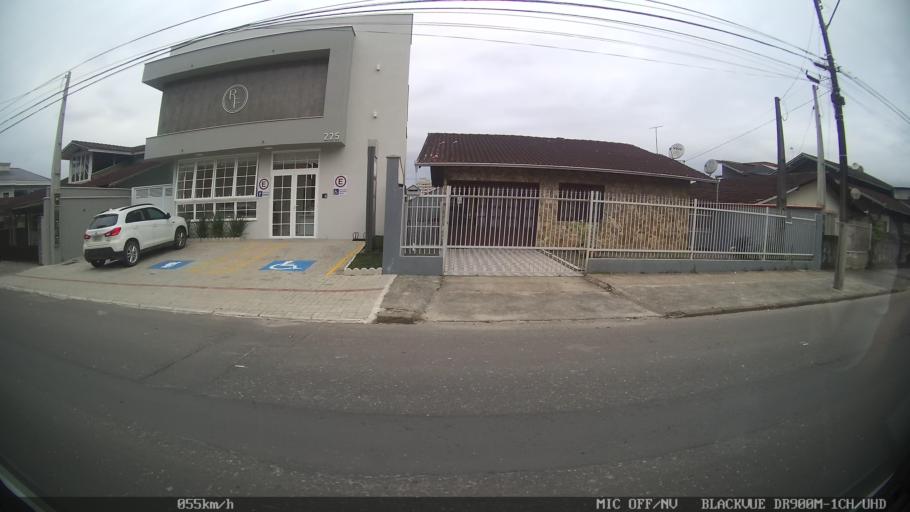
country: BR
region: Santa Catarina
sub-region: Joinville
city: Joinville
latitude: -26.2764
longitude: -48.8751
